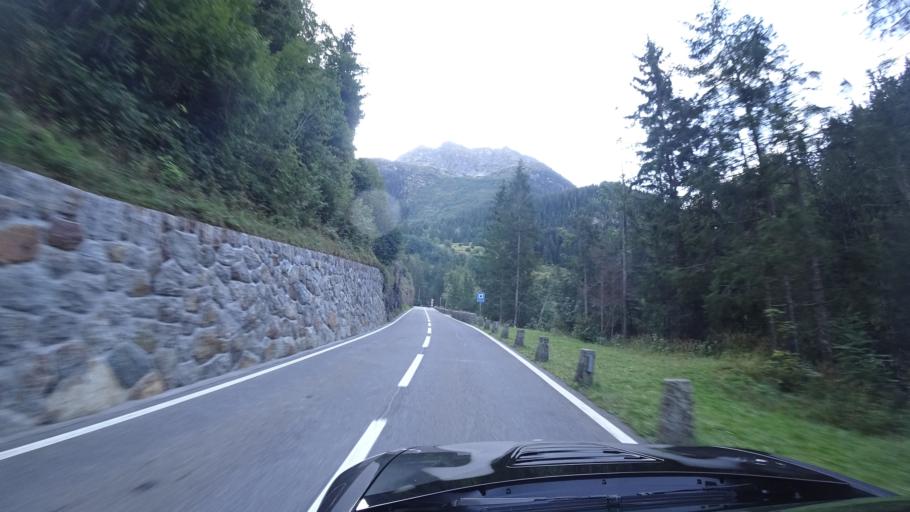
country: CH
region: Obwalden
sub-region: Obwalden
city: Engelberg
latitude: 46.7237
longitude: 8.3224
